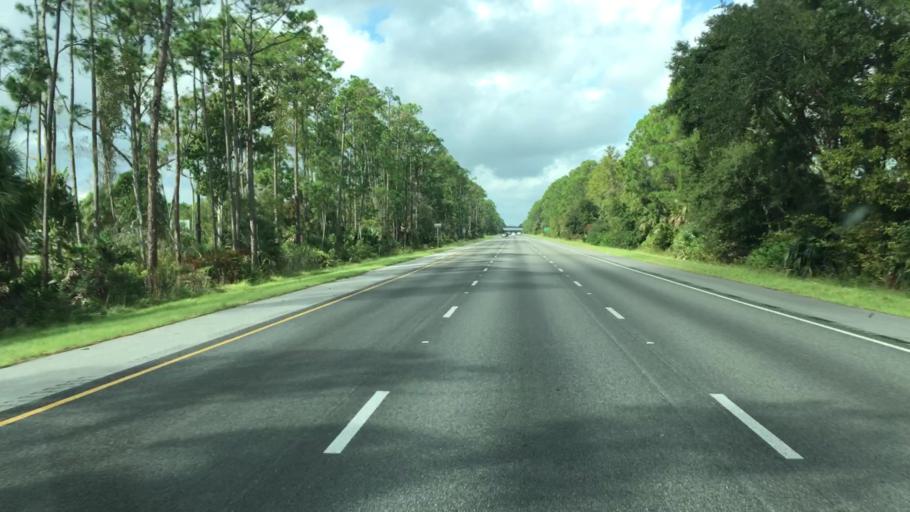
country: US
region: Florida
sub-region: Volusia County
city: Port Orange
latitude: 29.1150
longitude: -81.0354
